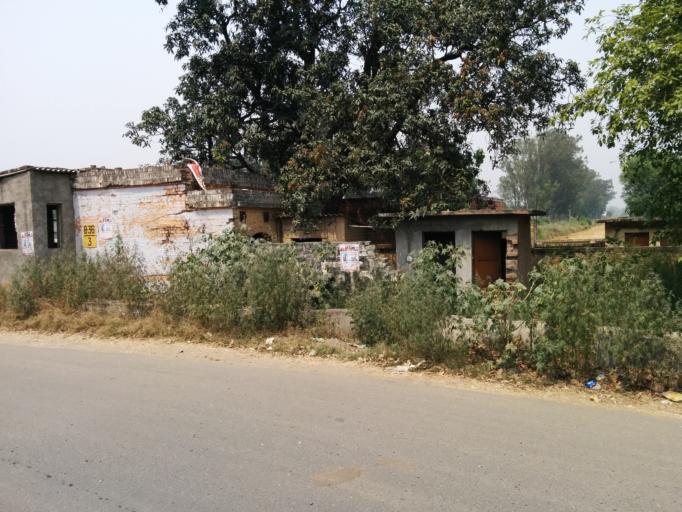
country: IN
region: Punjab
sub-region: Gurdaspur
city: Dhariwal
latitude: 31.9355
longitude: 75.3074
